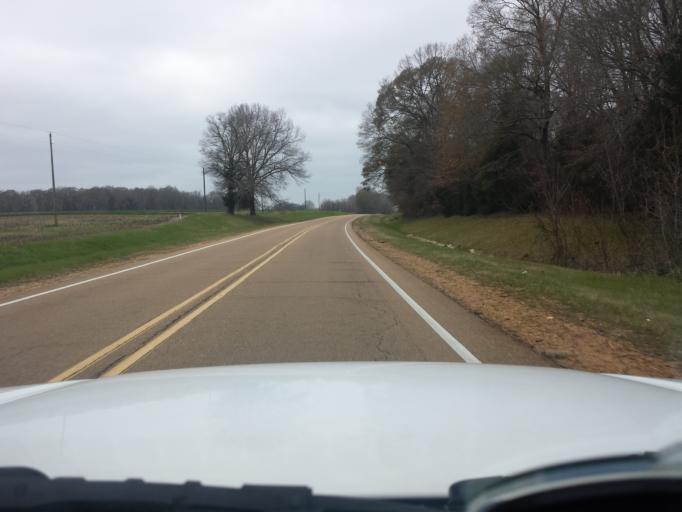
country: US
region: Mississippi
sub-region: Madison County
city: Canton
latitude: 32.7694
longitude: -90.1779
